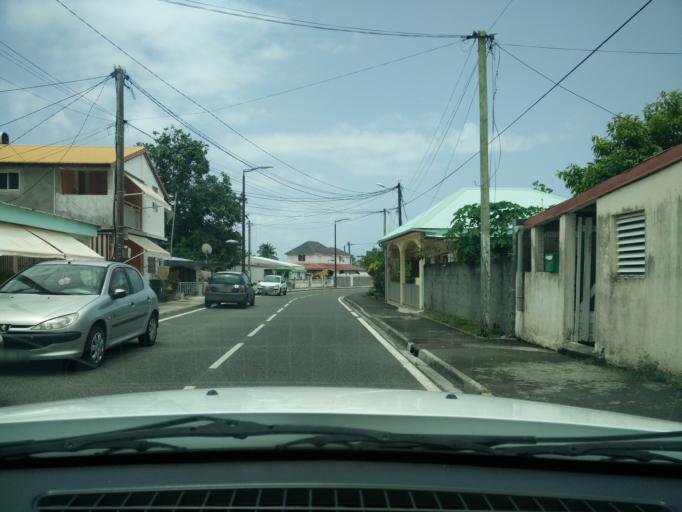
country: GP
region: Guadeloupe
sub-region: Guadeloupe
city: Capesterre-Belle-Eau
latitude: 16.0527
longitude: -61.5591
